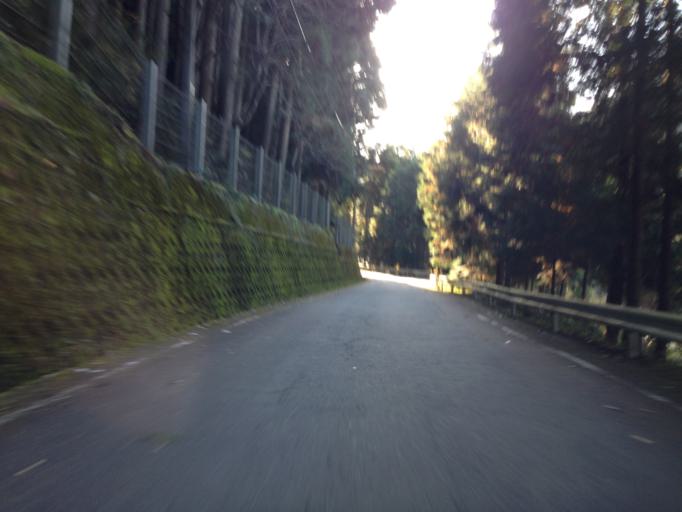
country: JP
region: Gifu
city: Mitake
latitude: 35.6092
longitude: 137.1834
